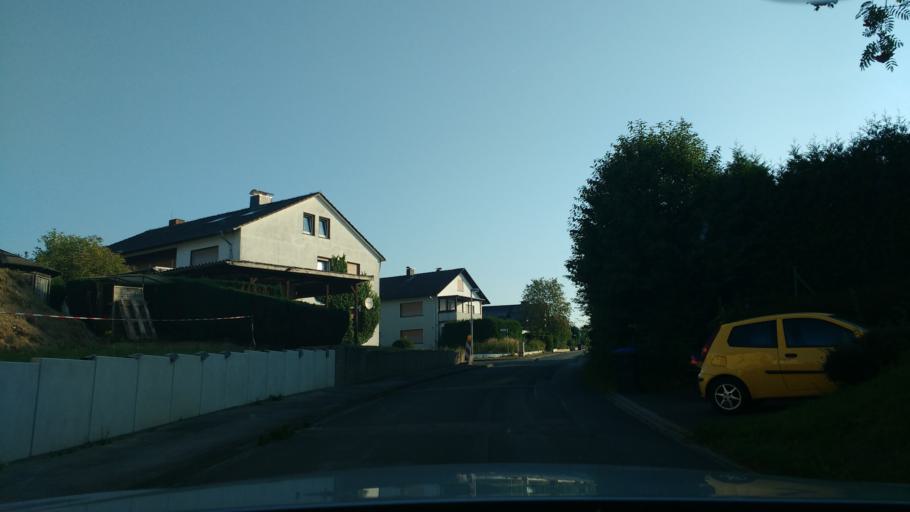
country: DE
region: North Rhine-Westphalia
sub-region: Regierungsbezirk Detmold
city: Dorentrup
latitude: 52.0290
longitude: 9.0588
